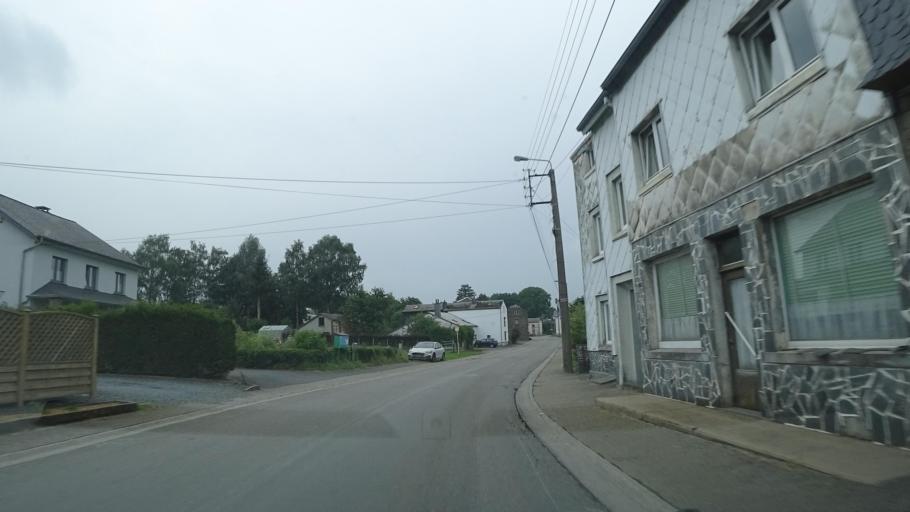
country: BE
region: Wallonia
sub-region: Province du Luxembourg
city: Bertrix
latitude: 49.8327
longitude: 5.3006
